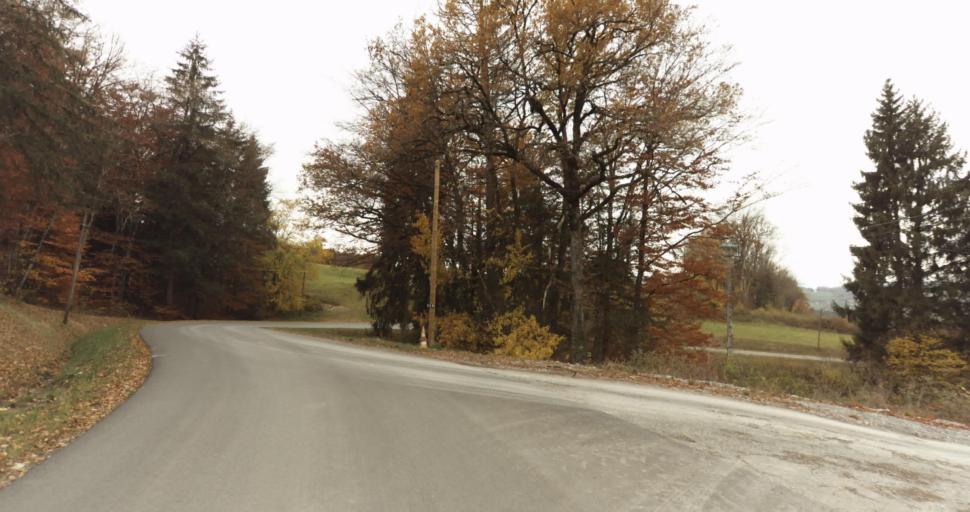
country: FR
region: Rhone-Alpes
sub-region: Departement de la Haute-Savoie
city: Groisy
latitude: 45.9932
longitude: 6.1958
